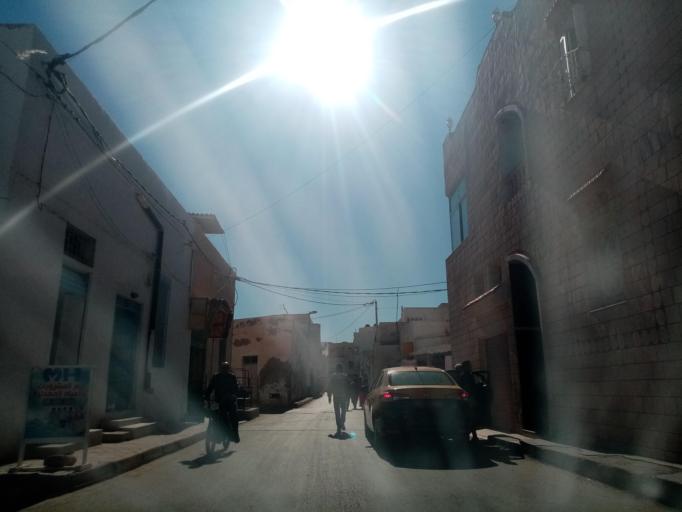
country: TN
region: Qabis
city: Gabes
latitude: 33.8797
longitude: 10.0897
